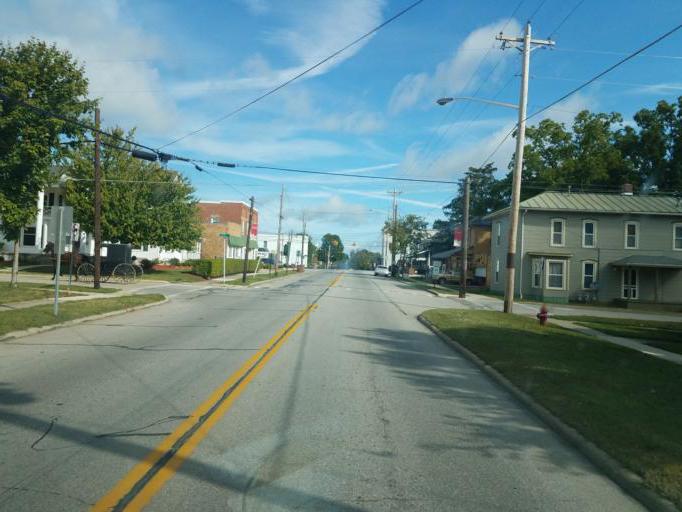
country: US
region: Ohio
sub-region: Lorain County
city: Wellington
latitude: 41.0991
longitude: -82.1233
